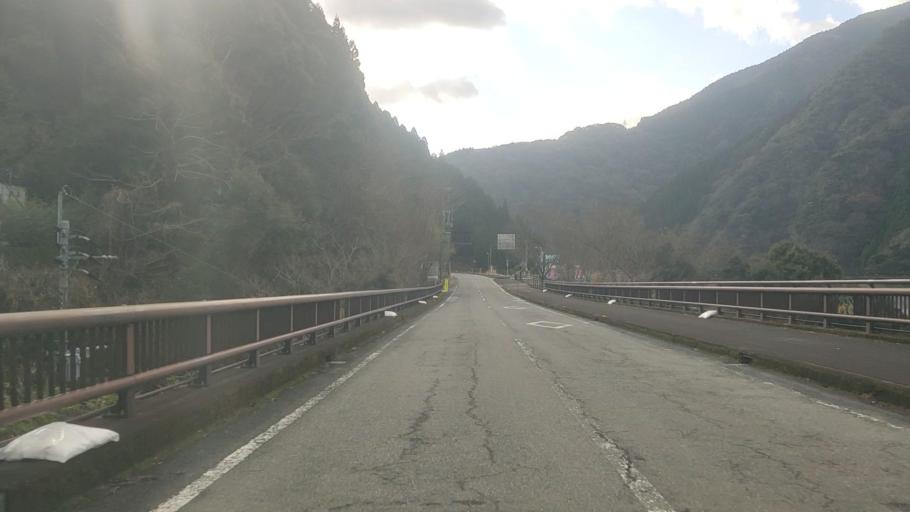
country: JP
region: Kumamoto
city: Hitoyoshi
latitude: 32.3956
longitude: 130.8268
